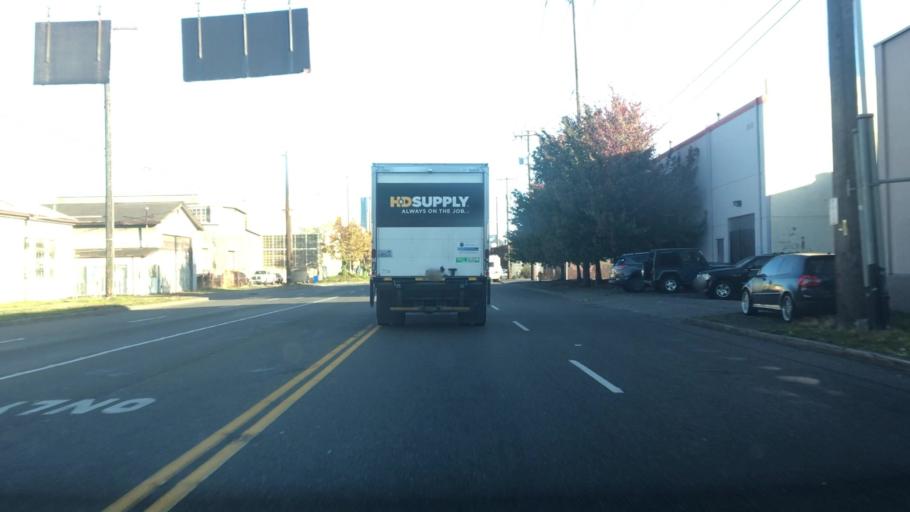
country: US
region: Washington
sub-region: King County
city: Seattle
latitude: 47.5722
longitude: -122.3259
